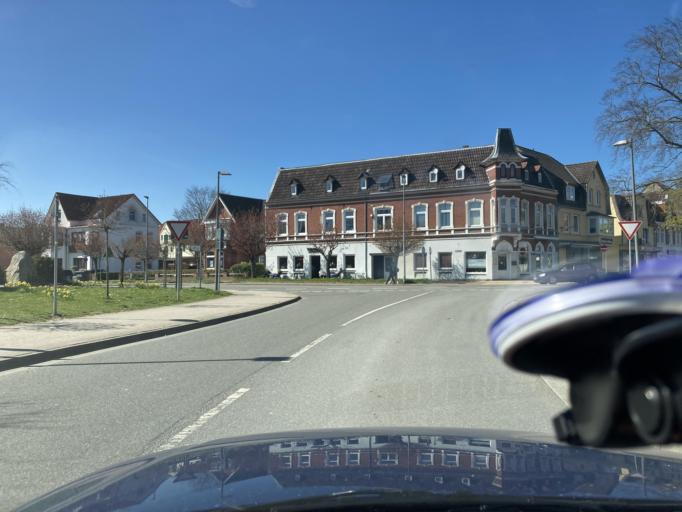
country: DE
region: Schleswig-Holstein
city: Heide
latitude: 54.1939
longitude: 9.0984
